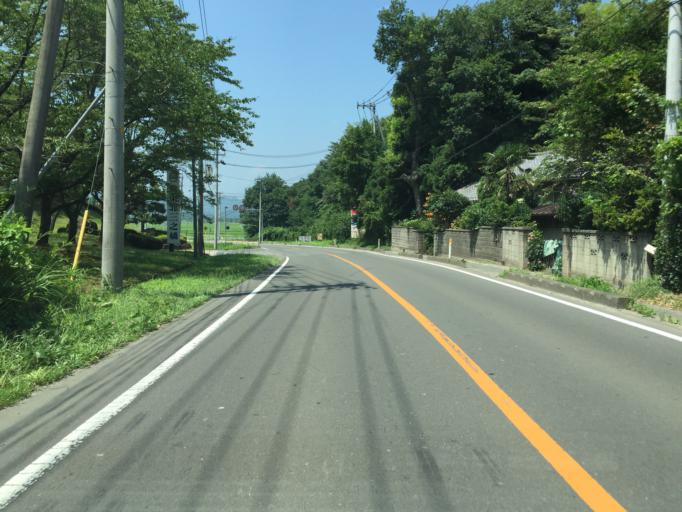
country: JP
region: Miyagi
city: Marumori
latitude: 37.9084
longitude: 140.7897
